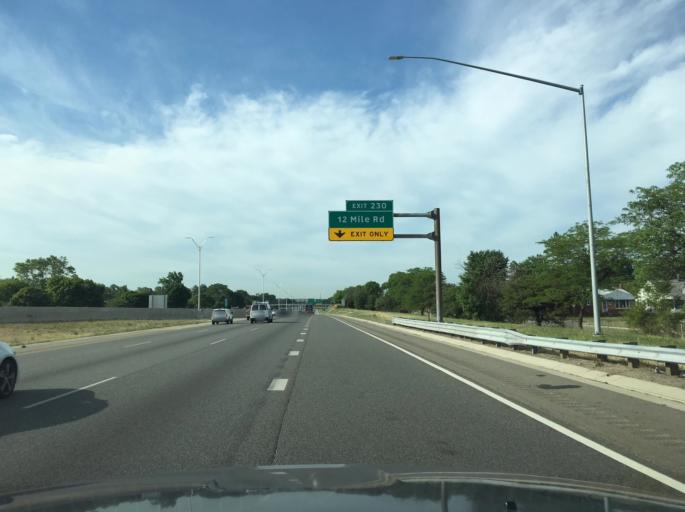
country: US
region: Michigan
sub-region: Macomb County
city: Roseville
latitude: 42.5169
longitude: -82.9188
